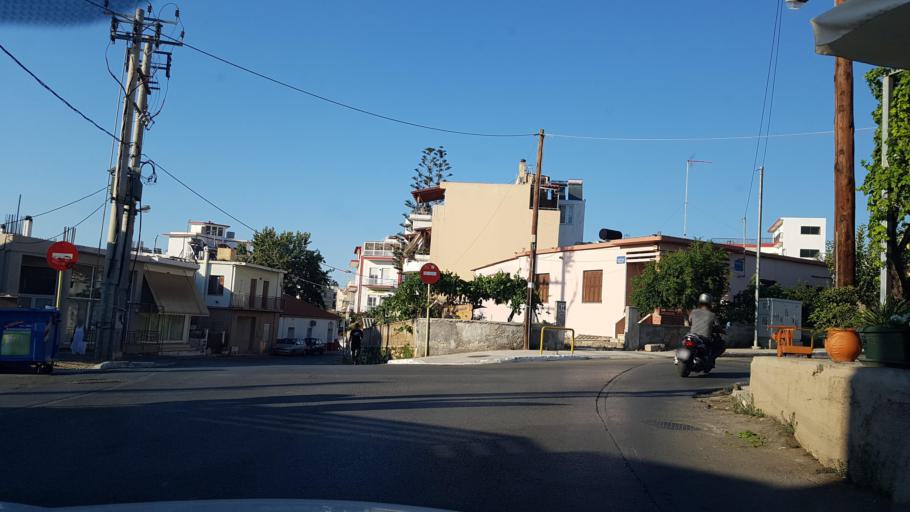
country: GR
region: Crete
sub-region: Nomos Chanias
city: Chania
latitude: 35.5074
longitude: 24.0090
